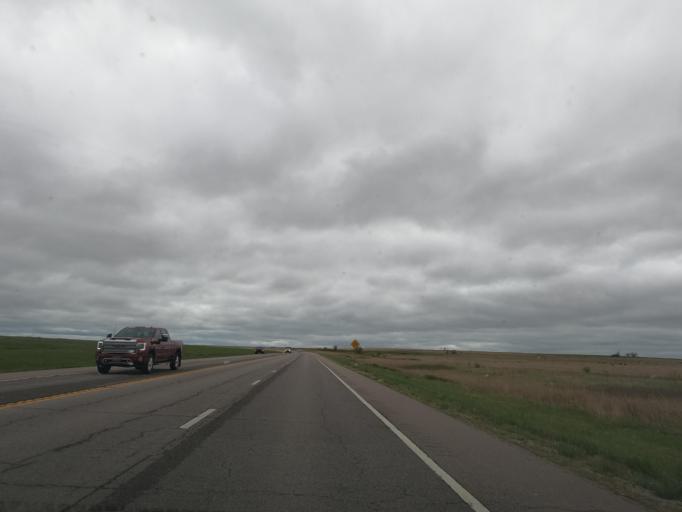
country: US
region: Kansas
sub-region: Greenwood County
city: Eureka
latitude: 37.6470
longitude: -96.4504
